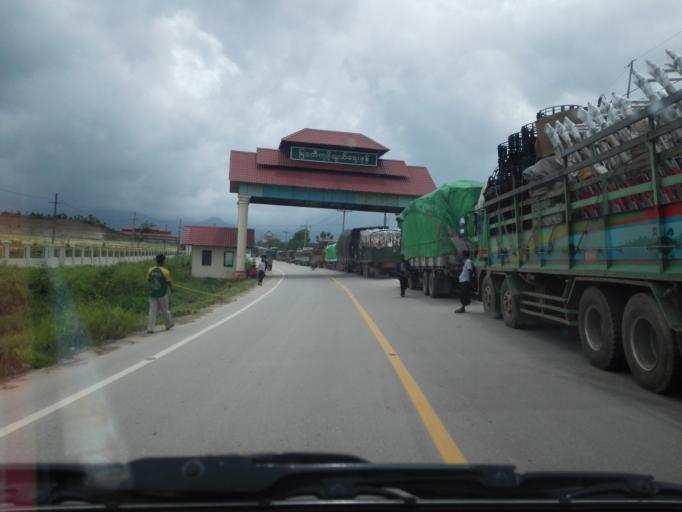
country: TH
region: Tak
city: Mae Sot
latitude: 16.6955
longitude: 98.4284
